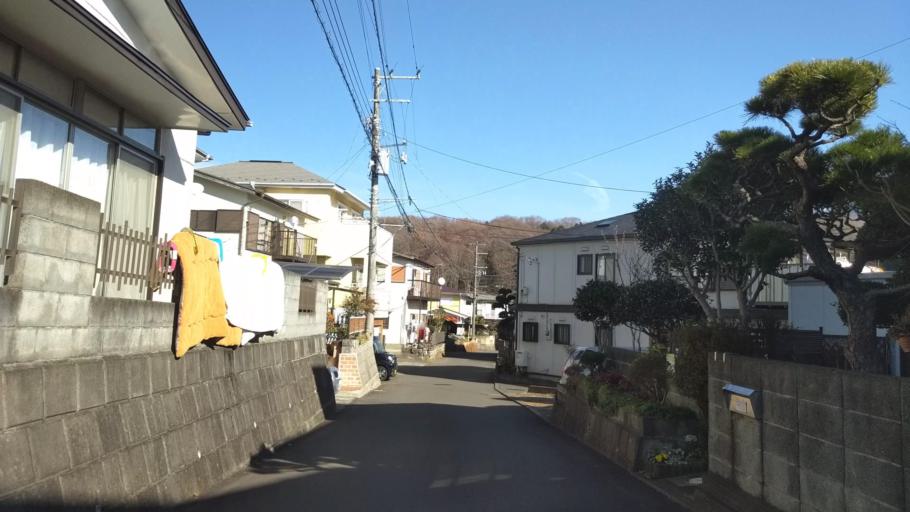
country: JP
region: Kanagawa
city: Hadano
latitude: 35.3432
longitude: 139.2345
